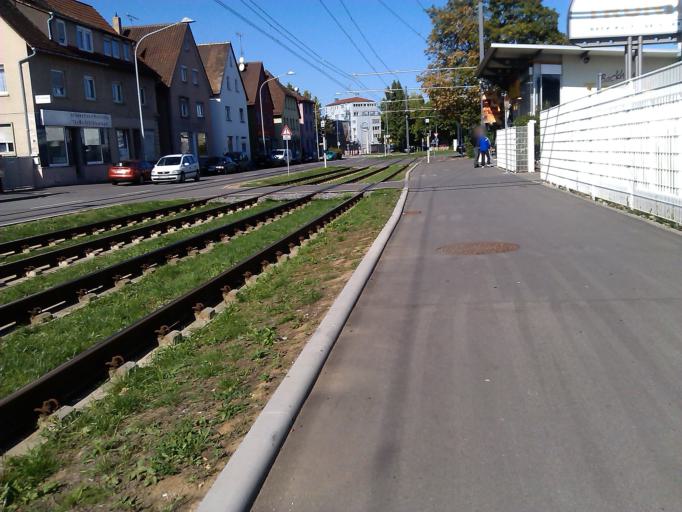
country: DE
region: Baden-Wuerttemberg
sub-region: Regierungsbezirk Stuttgart
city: Heilbronn
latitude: 49.1532
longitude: 9.2189
